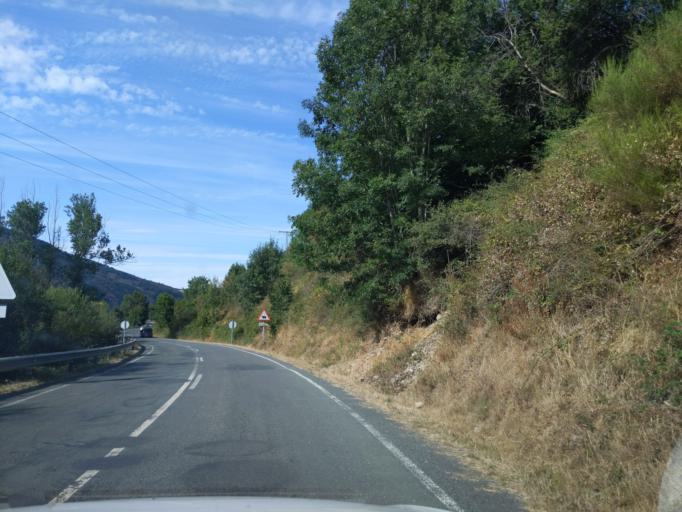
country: ES
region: La Rioja
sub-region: Provincia de La Rioja
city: Zorraquin
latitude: 42.2837
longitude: -3.0266
